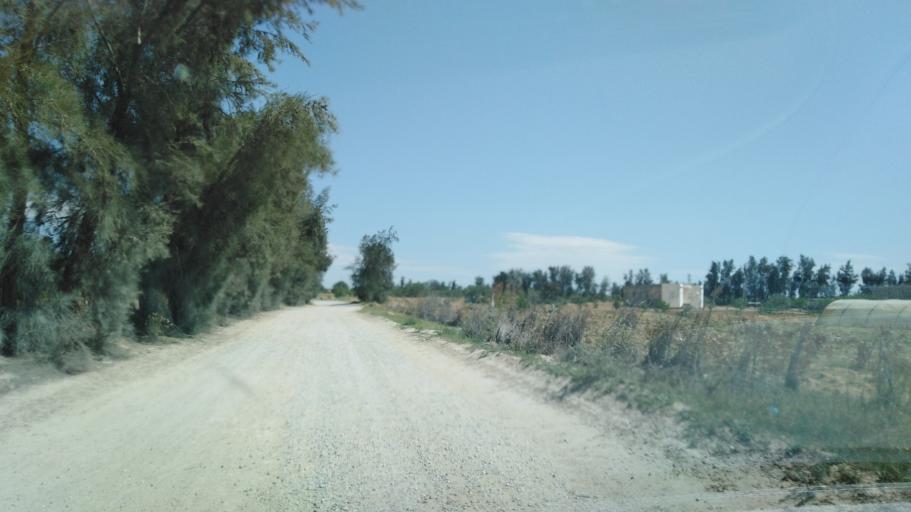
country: TN
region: Safaqis
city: Sfax
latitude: 34.7553
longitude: 10.5295
